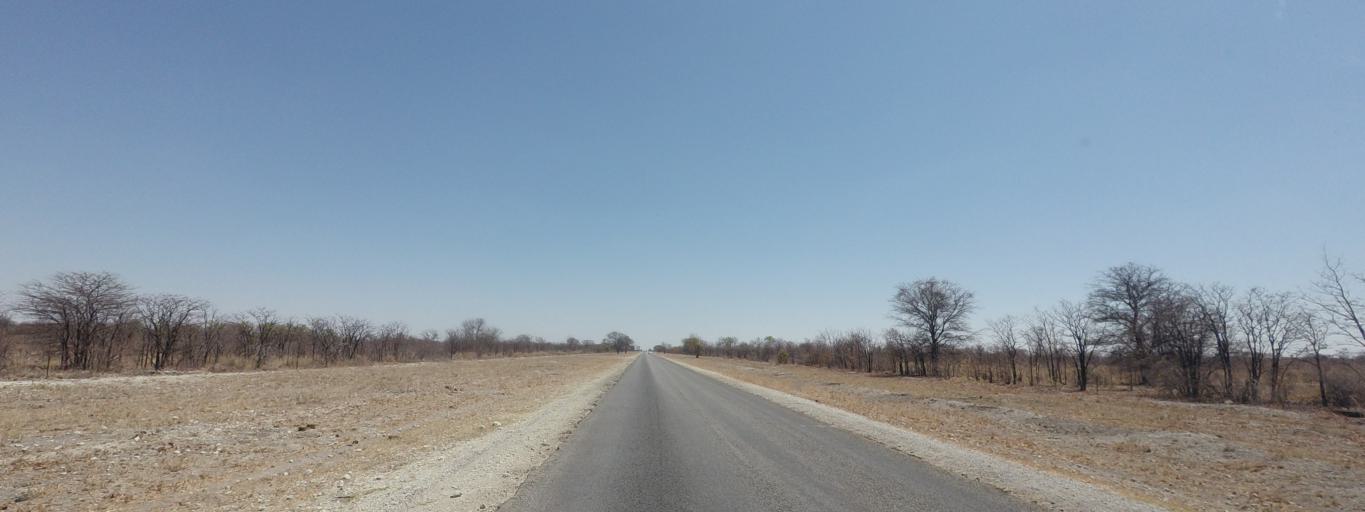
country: BW
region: Central
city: Nata
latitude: -20.3630
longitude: 26.3193
